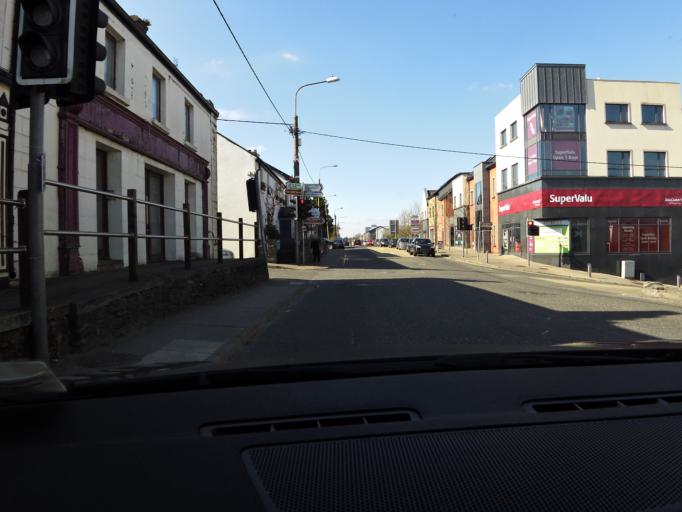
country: IE
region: Connaught
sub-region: County Galway
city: Moycullen
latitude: 53.3376
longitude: -9.1800
